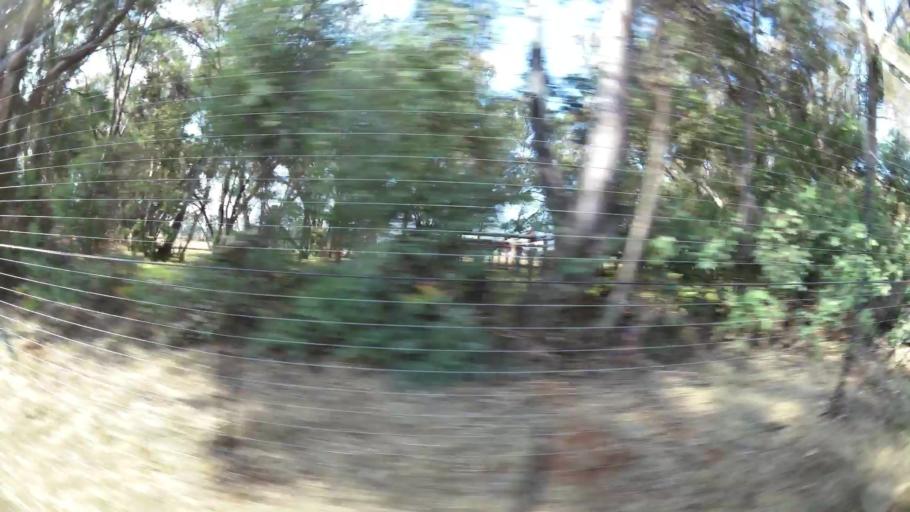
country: ZA
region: Gauteng
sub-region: Ekurhuleni Metropolitan Municipality
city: Benoni
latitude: -26.0828
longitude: 28.3607
